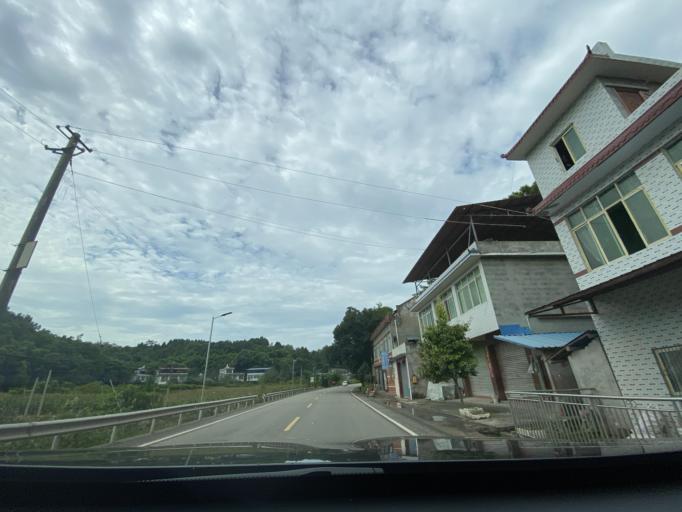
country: CN
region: Sichuan
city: Jiancheng
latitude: 30.4771
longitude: 104.6302
